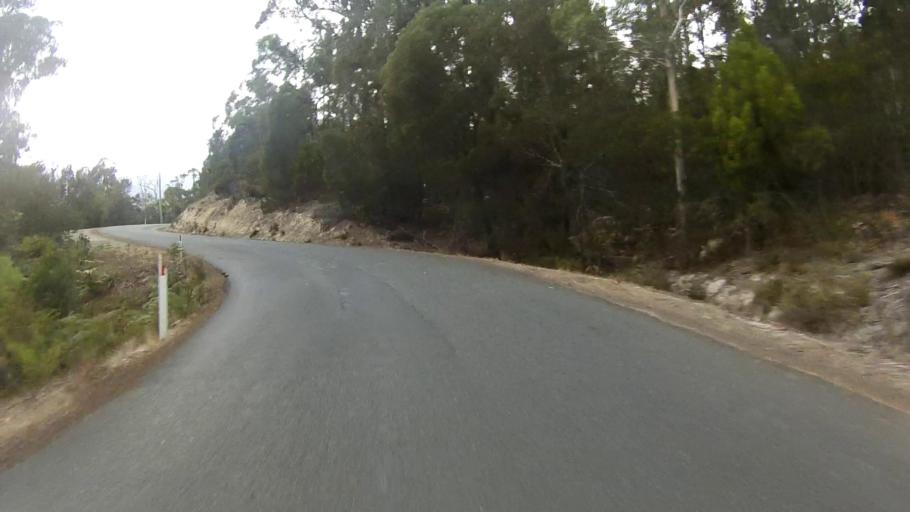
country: AU
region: Tasmania
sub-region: Huon Valley
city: Cygnet
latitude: -43.2158
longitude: 147.1006
